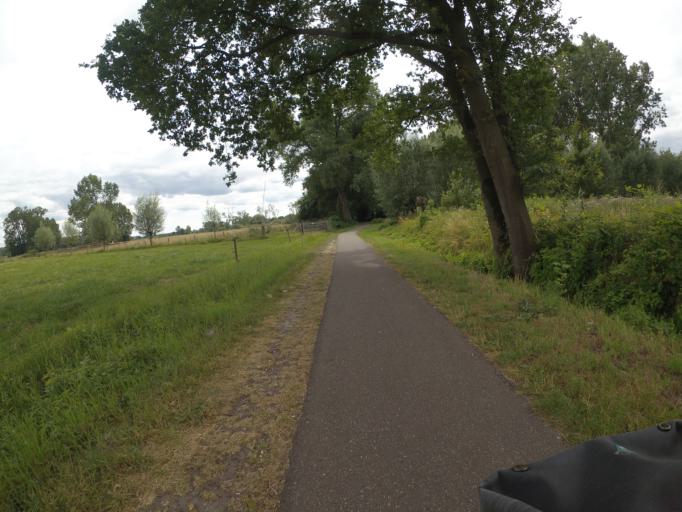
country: NL
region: North Brabant
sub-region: Gemeente Son en Breugel
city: Son
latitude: 51.4886
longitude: 5.5054
